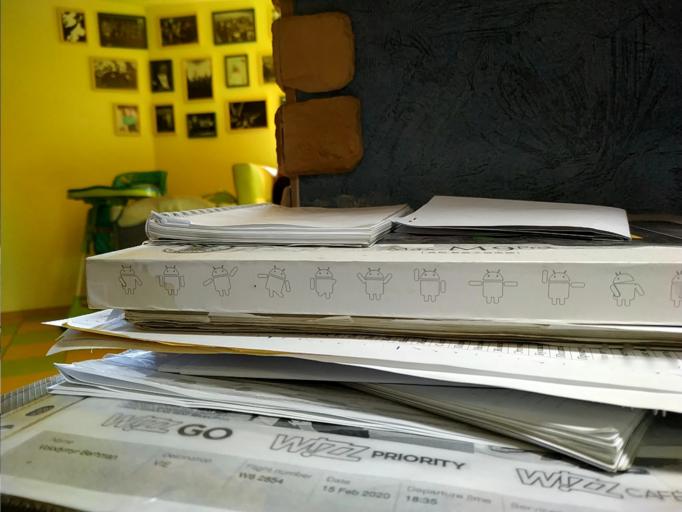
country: RU
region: Pskov
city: Plyussa
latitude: 58.4878
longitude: 29.5710
